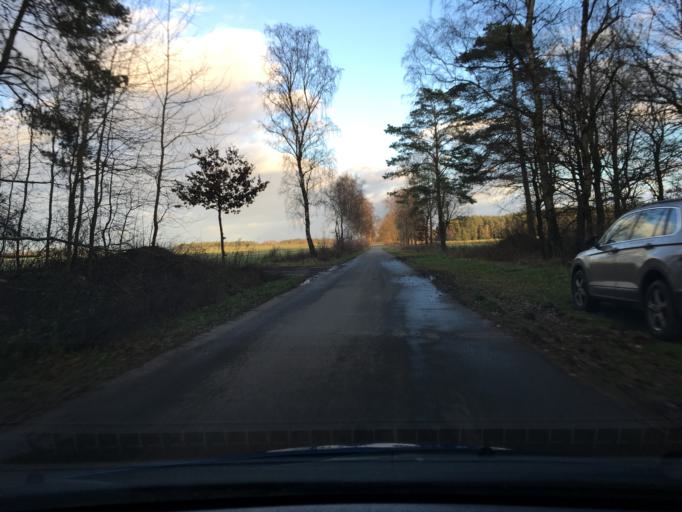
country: DE
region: Lower Saxony
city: Soderstorf
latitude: 53.1120
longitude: 10.1547
